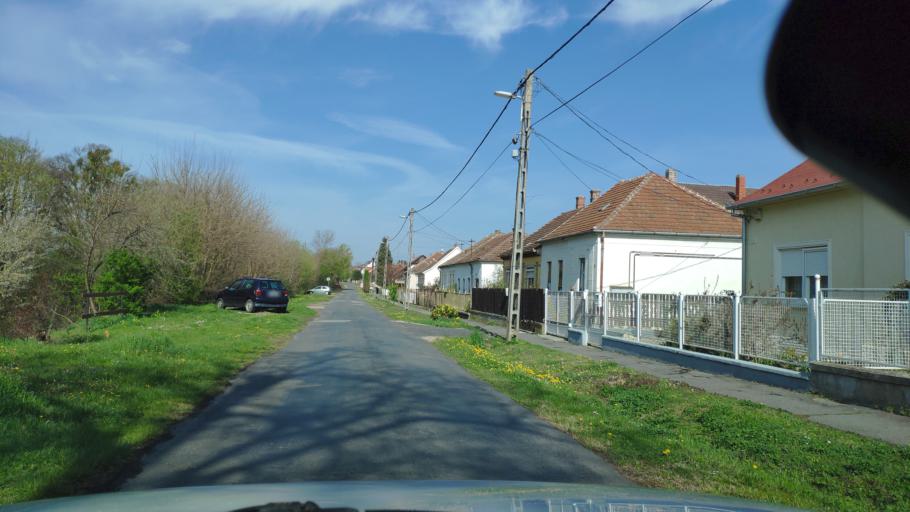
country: HU
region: Zala
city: Nagykanizsa
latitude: 46.4488
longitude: 17.0054
